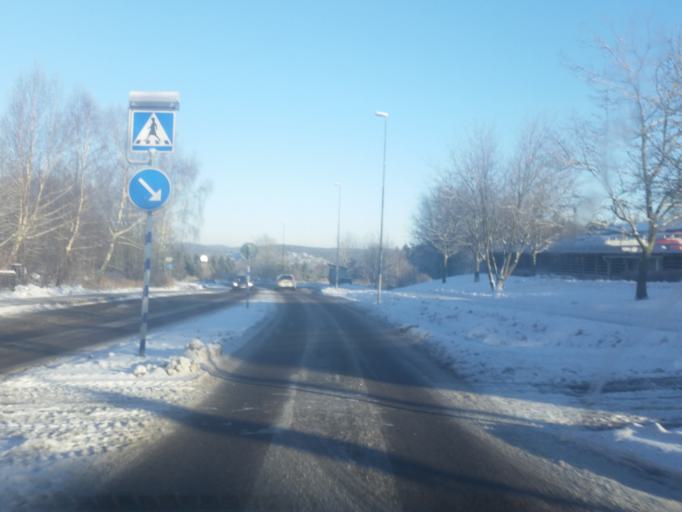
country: SE
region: Vaestra Goetaland
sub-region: Partille Kommun
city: Furulund
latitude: 57.7256
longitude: 12.1339
